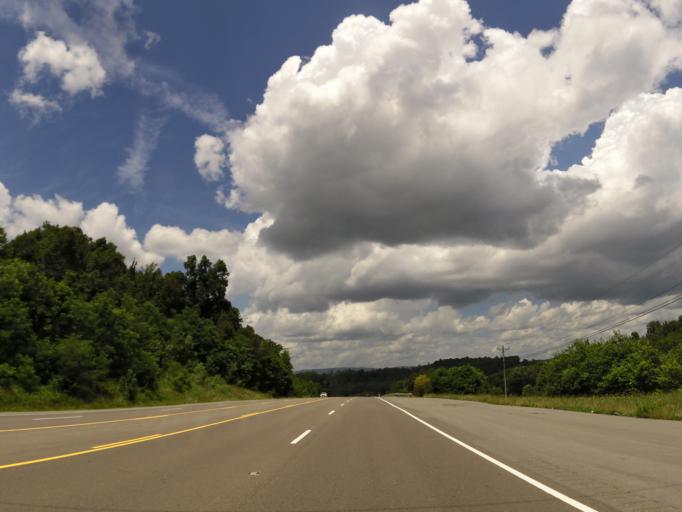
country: US
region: Tennessee
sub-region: Claiborne County
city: Tazewell
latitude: 36.4960
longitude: -83.5929
